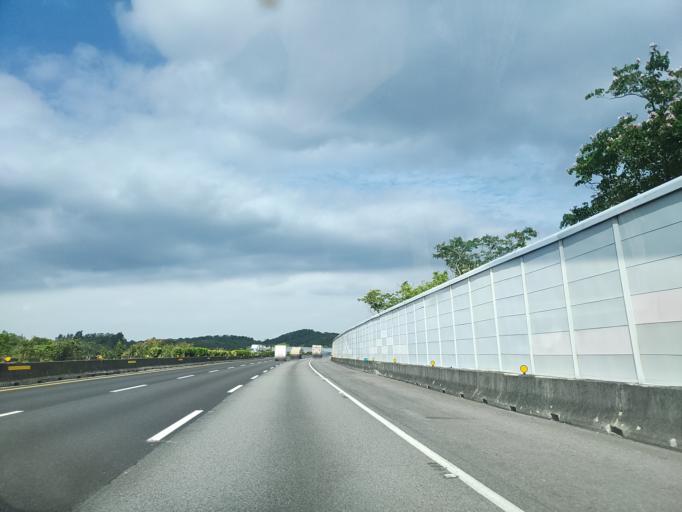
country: TW
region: Taiwan
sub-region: Miaoli
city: Miaoli
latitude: 24.6321
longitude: 120.8663
